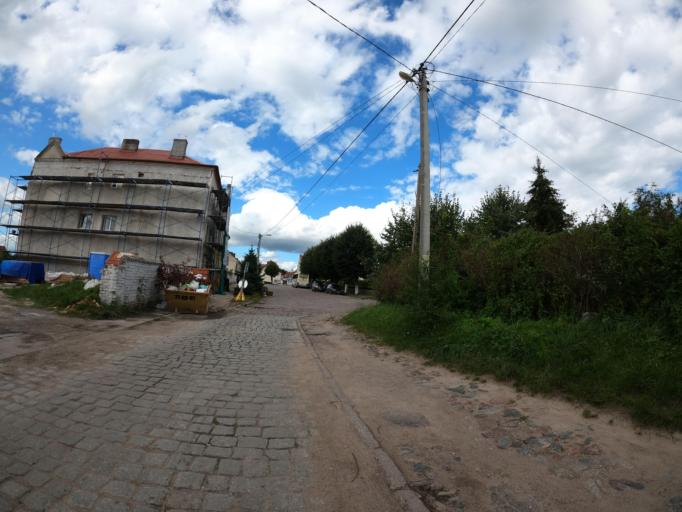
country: RU
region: Kaliningrad
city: Zheleznodorozhnyy
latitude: 54.3600
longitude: 21.3053
